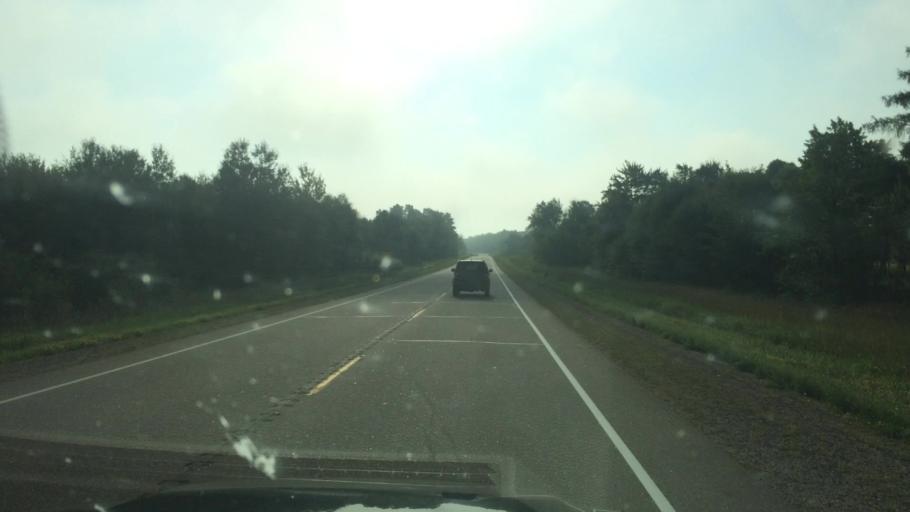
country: US
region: Wisconsin
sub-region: Langlade County
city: Antigo
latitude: 45.1449
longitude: -89.3120
